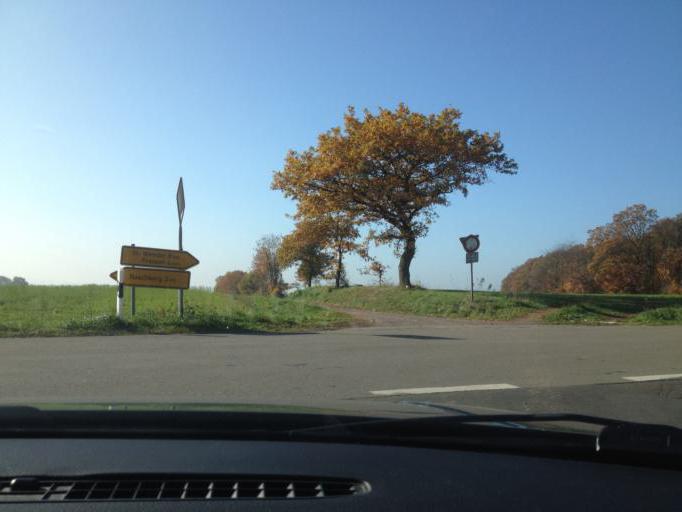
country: DE
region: Rheinland-Pfalz
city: Hahnweiler
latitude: 49.5194
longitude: 7.2001
